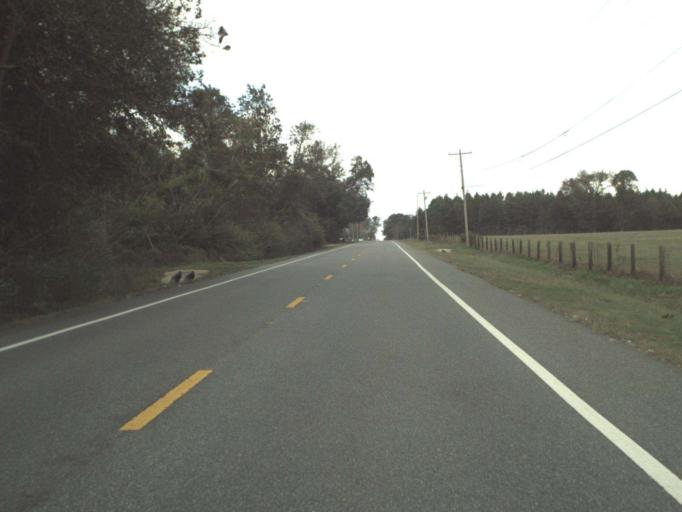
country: US
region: Florida
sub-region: Santa Rosa County
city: Point Baker
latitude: 30.8286
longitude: -87.0478
